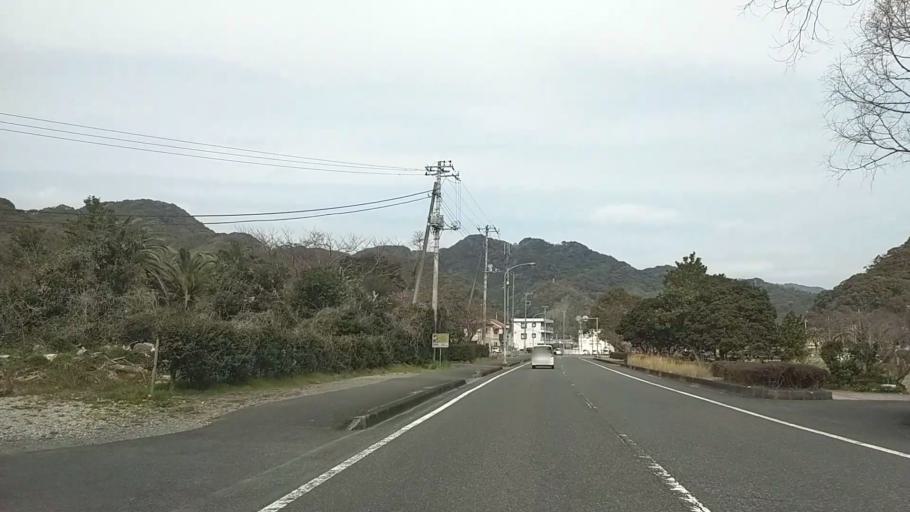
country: JP
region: Shizuoka
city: Shimoda
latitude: 34.6973
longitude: 138.9402
